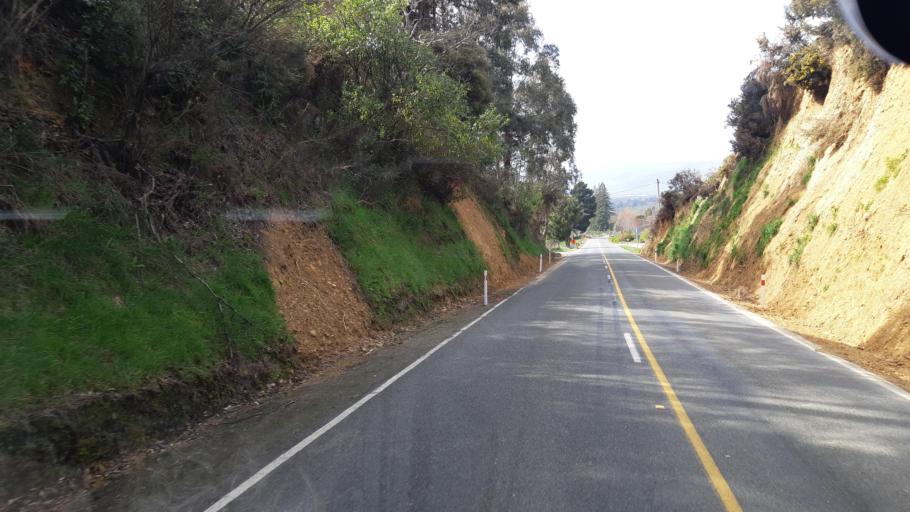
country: NZ
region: Tasman
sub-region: Tasman District
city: Mapua
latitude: -41.2984
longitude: 173.0577
